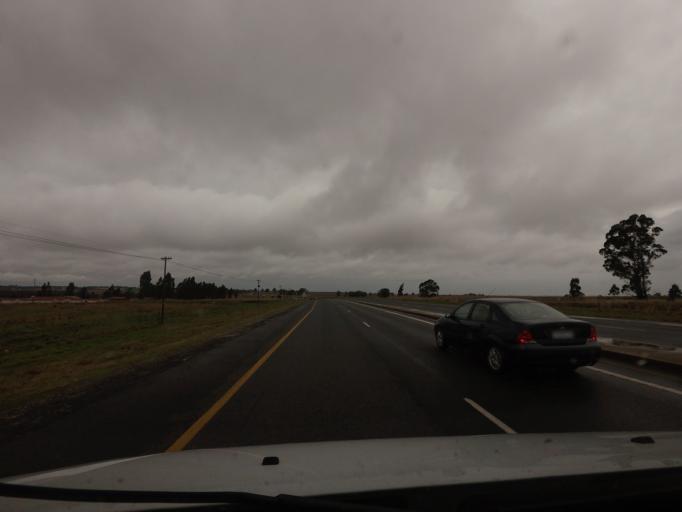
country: ZA
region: Mpumalanga
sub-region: Nkangala District Municipality
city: Belfast
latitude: -25.7643
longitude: 29.9701
